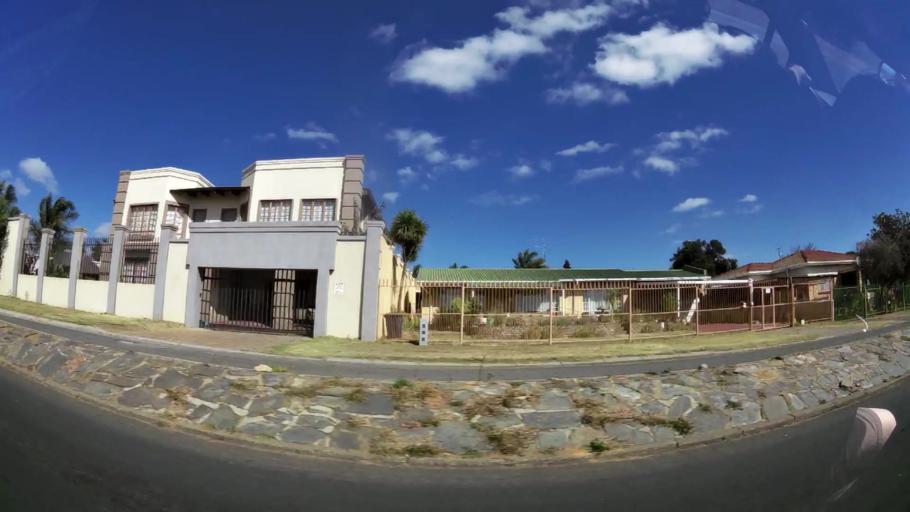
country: ZA
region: Gauteng
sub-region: West Rand District Municipality
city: Krugersdorp
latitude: -26.1158
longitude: 27.7986
